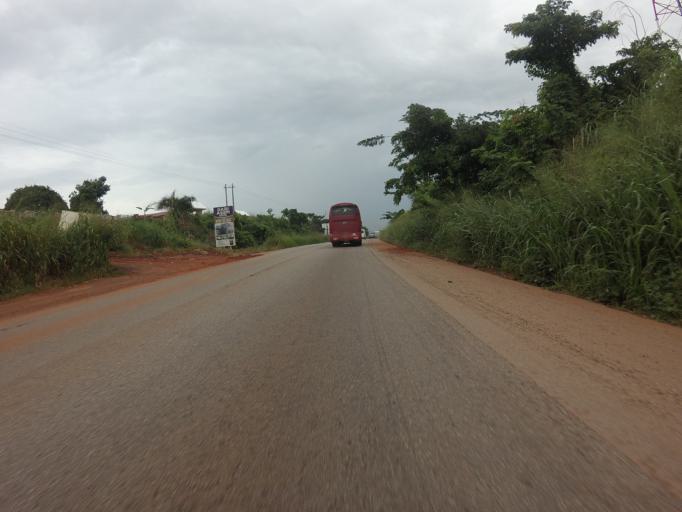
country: GH
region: Ashanti
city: Konongo
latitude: 6.6178
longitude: -1.1884
